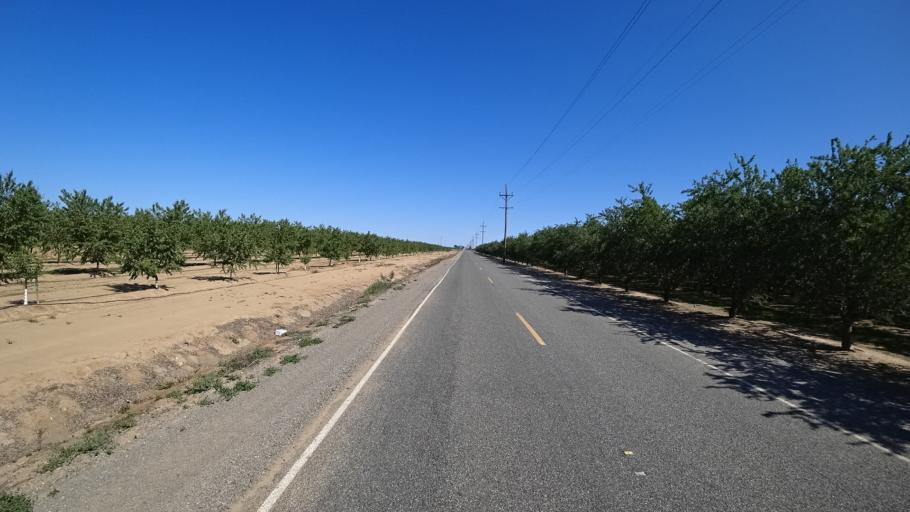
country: US
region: California
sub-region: Glenn County
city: Willows
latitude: 39.6287
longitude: -122.1787
